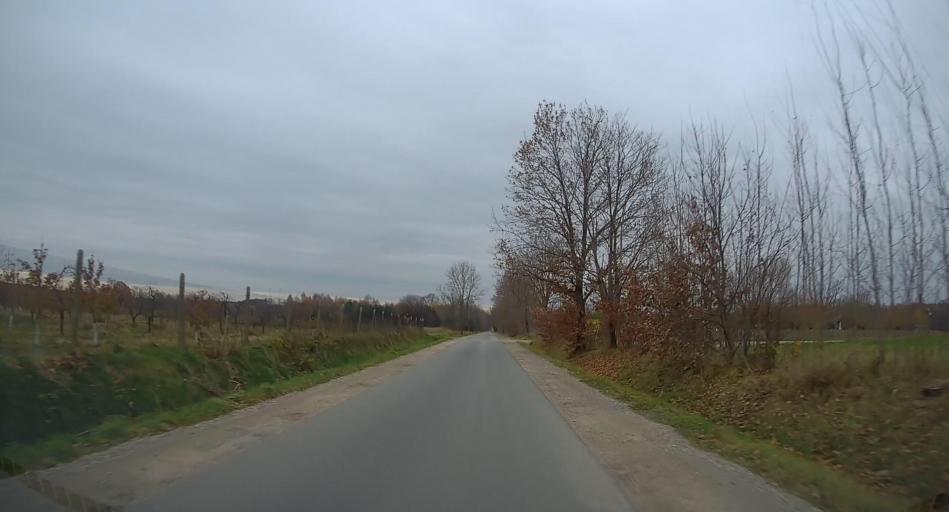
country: PL
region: Lodz Voivodeship
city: Zabia Wola
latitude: 52.0047
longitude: 20.6569
